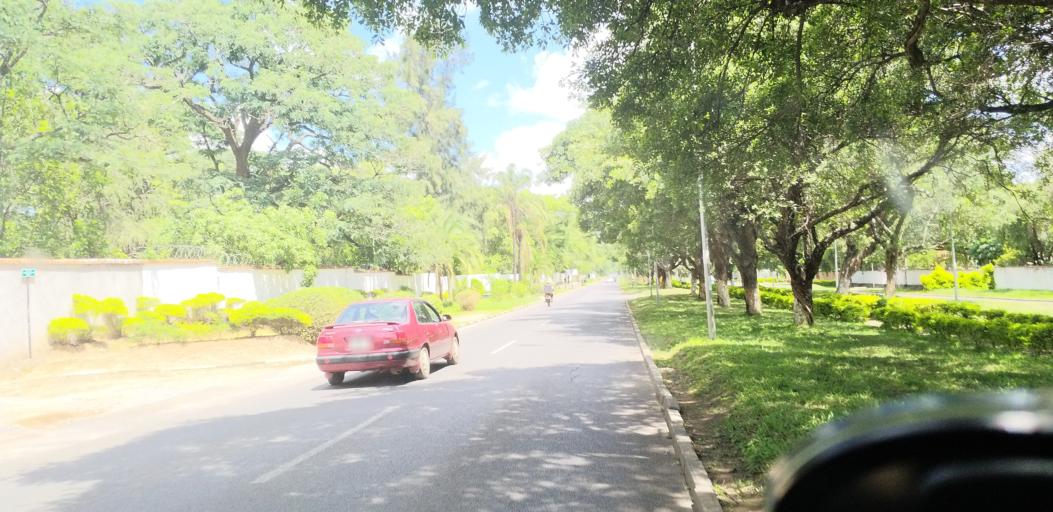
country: ZM
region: Lusaka
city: Lusaka
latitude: -15.4281
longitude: 28.3199
